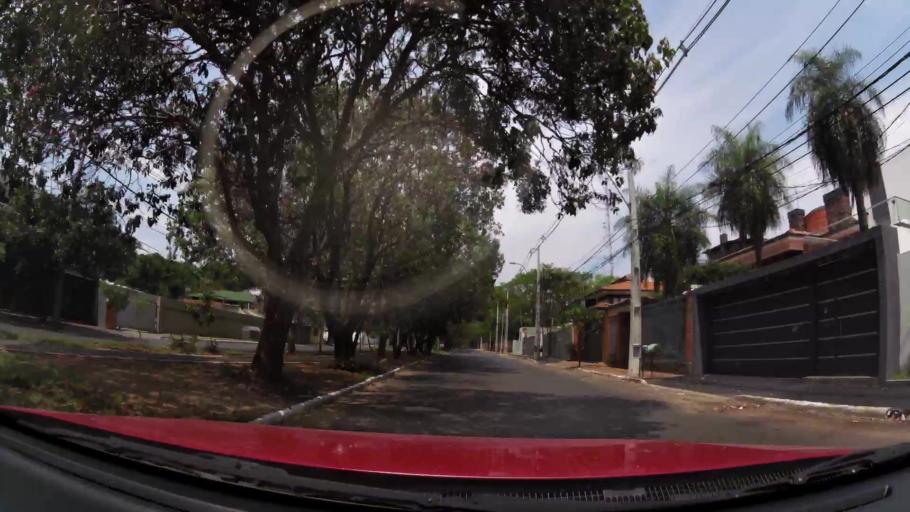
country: PY
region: Central
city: Fernando de la Mora
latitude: -25.3072
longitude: -57.5650
